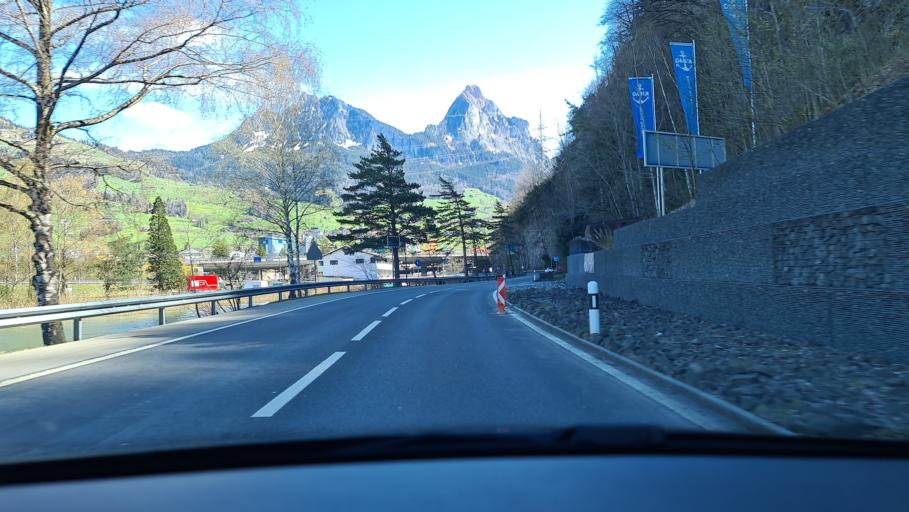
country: CH
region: Schwyz
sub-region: Bezirk Schwyz
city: Steinen
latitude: 47.0285
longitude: 8.6221
